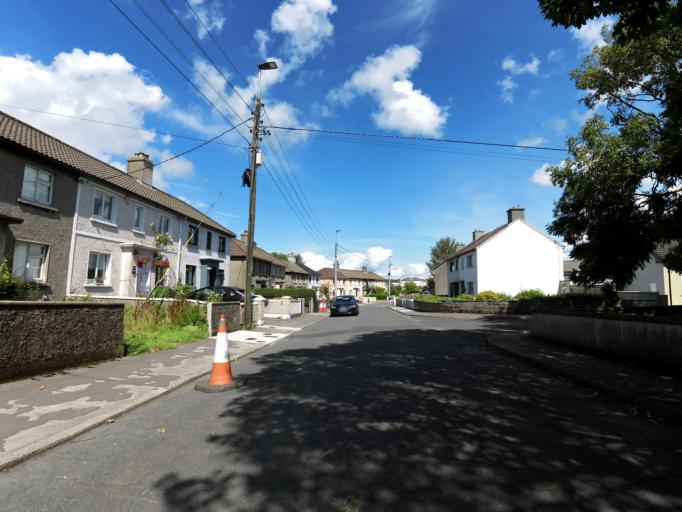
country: IE
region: Connaught
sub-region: County Galway
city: Gaillimh
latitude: 53.2739
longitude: -9.0677
